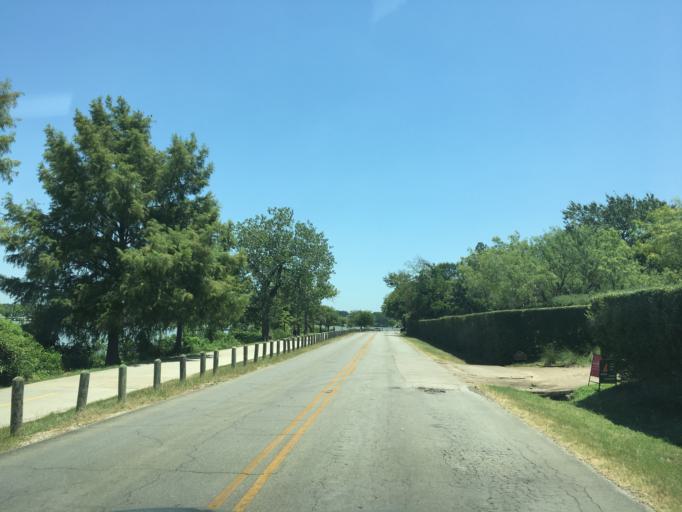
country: US
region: Texas
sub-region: Dallas County
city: Highland Park
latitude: 32.8379
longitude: -96.7263
